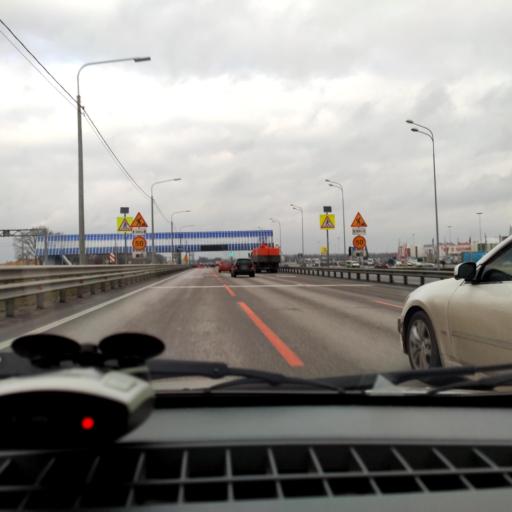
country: RU
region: Voronezj
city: Podgornoye
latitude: 51.7868
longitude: 39.1963
